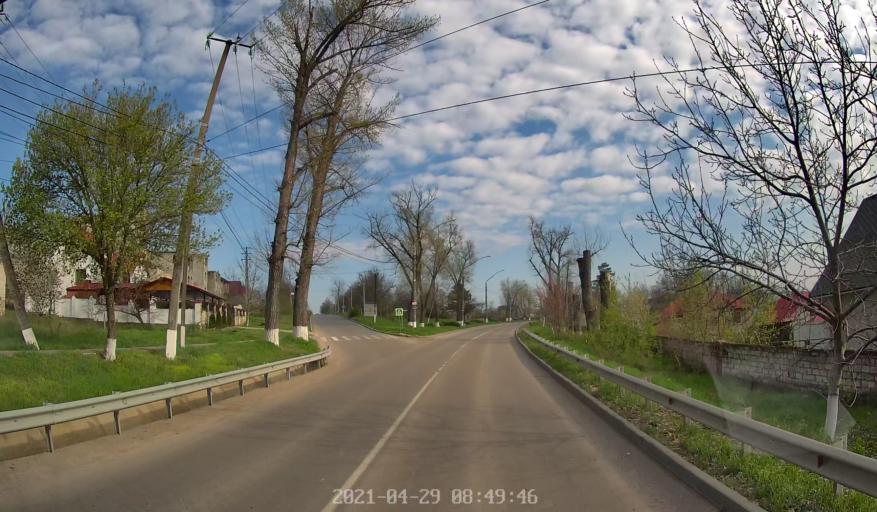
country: MD
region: Chisinau
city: Cricova
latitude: 47.1267
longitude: 28.8648
